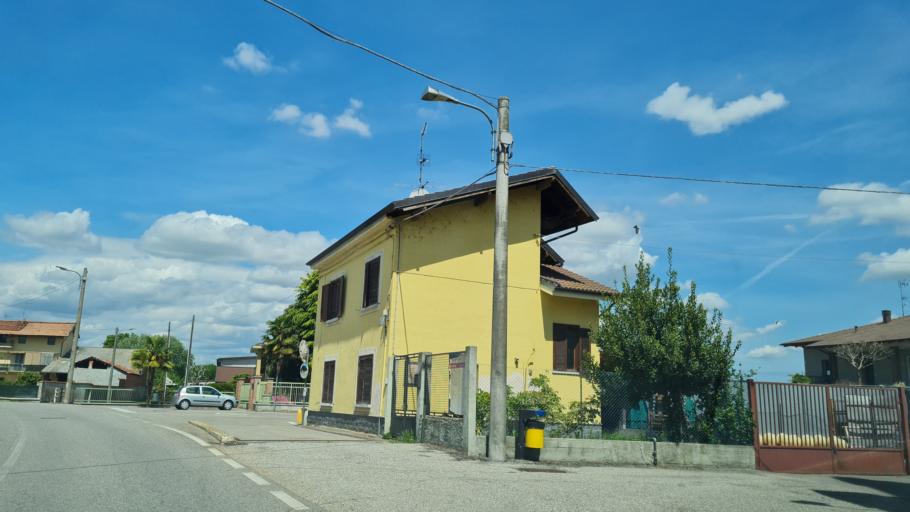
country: IT
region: Piedmont
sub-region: Provincia di Novara
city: Sillavengo
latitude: 45.5216
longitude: 8.4400
